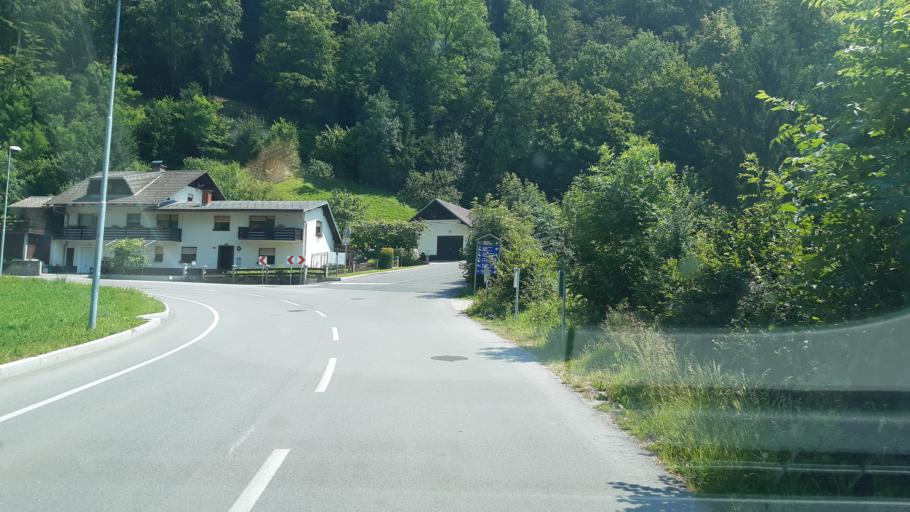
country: SI
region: Cerklje na Gorenjskem
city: Cerklje na Gorenjskem
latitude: 46.2650
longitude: 14.4939
